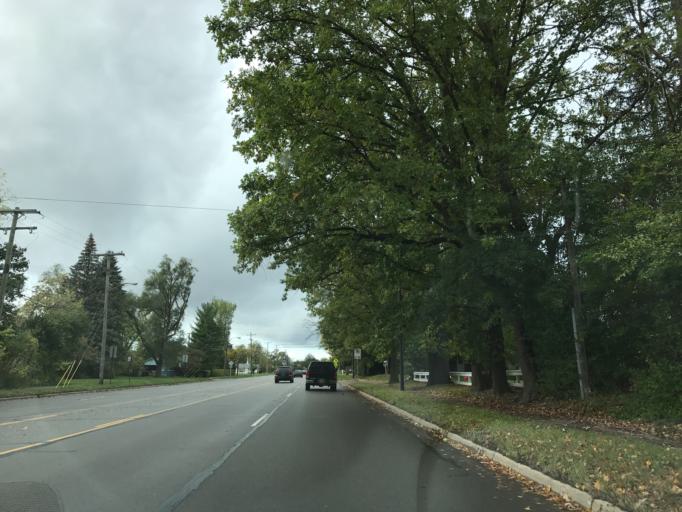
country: US
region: Michigan
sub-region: Washtenaw County
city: Ann Arbor
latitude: 42.2449
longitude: -83.7073
